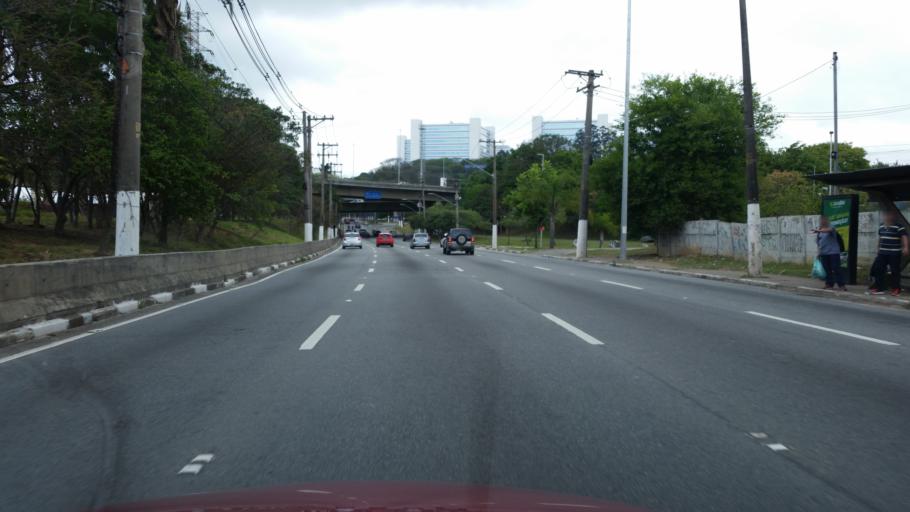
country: BR
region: Sao Paulo
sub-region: Taboao Da Serra
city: Taboao da Serra
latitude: -23.6429
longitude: -46.7272
